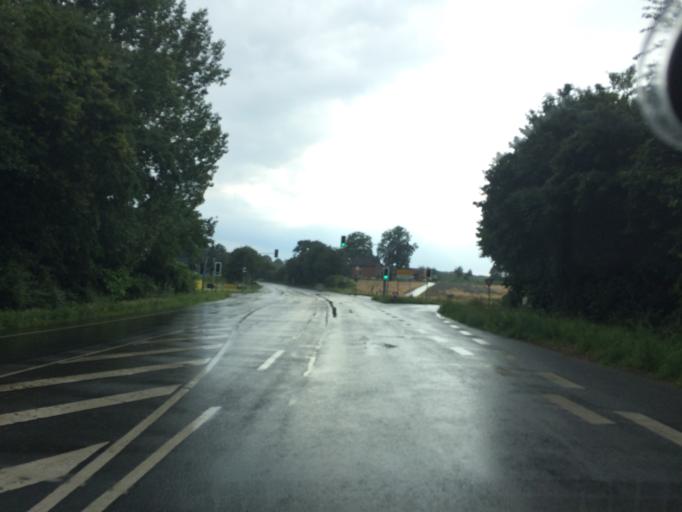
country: DE
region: North Rhine-Westphalia
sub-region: Regierungsbezirk Munster
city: Haltern
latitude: 51.7783
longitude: 7.2279
